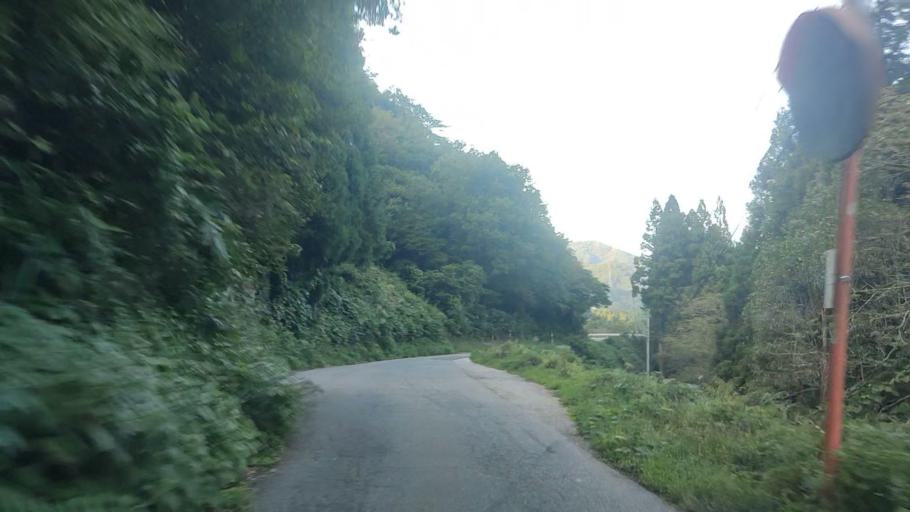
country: JP
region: Toyama
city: Yatsuomachi-higashikumisaka
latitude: 36.4986
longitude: 137.0641
